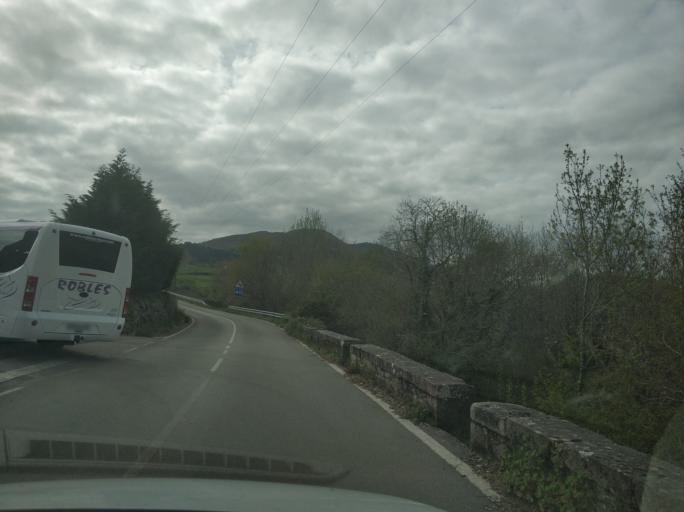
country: ES
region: Cantabria
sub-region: Provincia de Cantabria
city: Ruente
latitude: 43.2390
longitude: -4.2837
